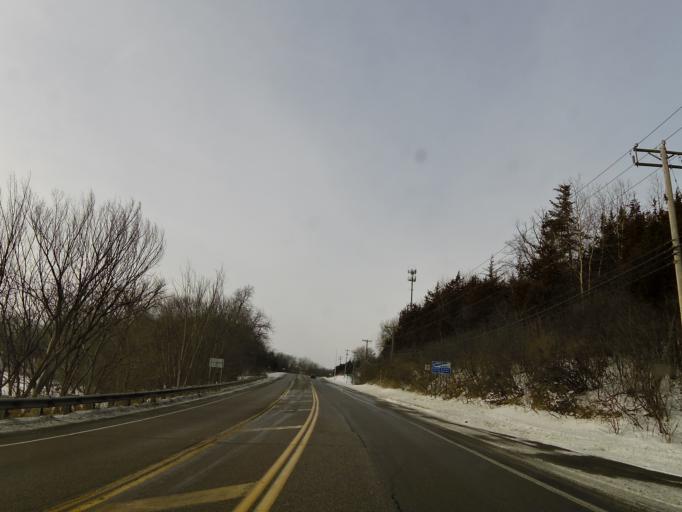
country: US
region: Minnesota
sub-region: Carver County
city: Victoria
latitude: 44.8915
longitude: -93.6637
